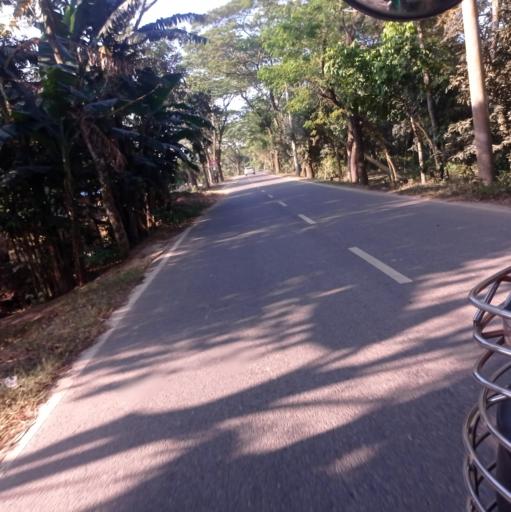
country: BD
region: Dhaka
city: Bajitpur
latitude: 24.1483
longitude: 90.8136
